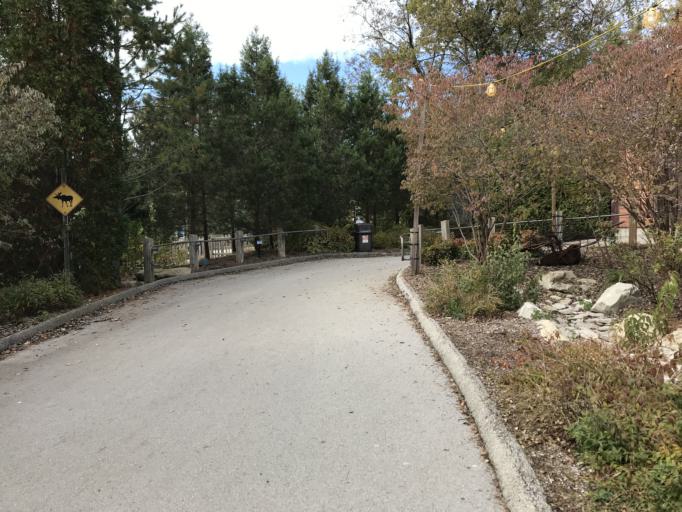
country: US
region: Kentucky
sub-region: Jefferson County
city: Audubon Park
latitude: 38.2042
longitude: -85.7036
